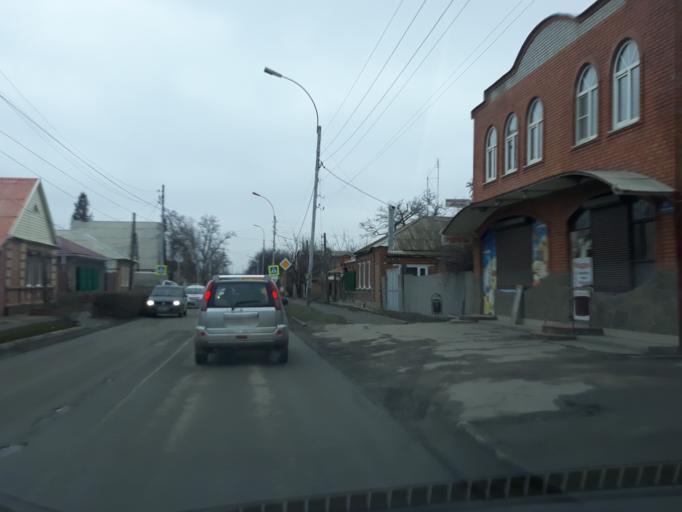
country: RU
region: Rostov
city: Taganrog
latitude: 47.2264
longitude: 38.9241
